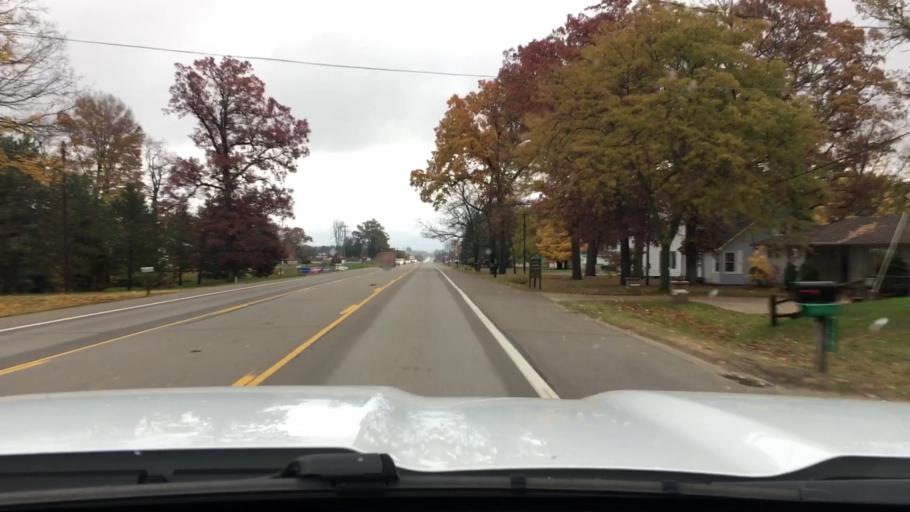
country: US
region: Michigan
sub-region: Montcalm County
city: Greenville
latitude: 43.1768
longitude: -85.3045
